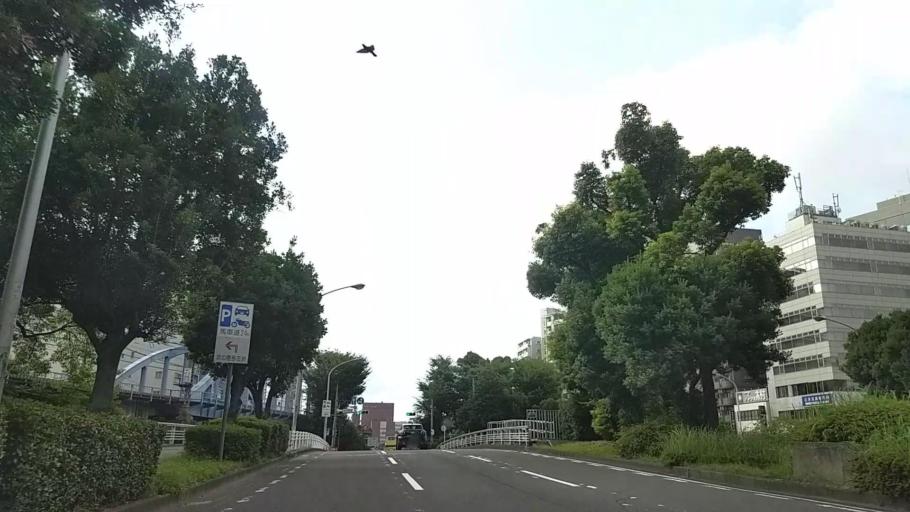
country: JP
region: Kanagawa
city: Yokohama
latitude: 35.4483
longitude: 139.6319
